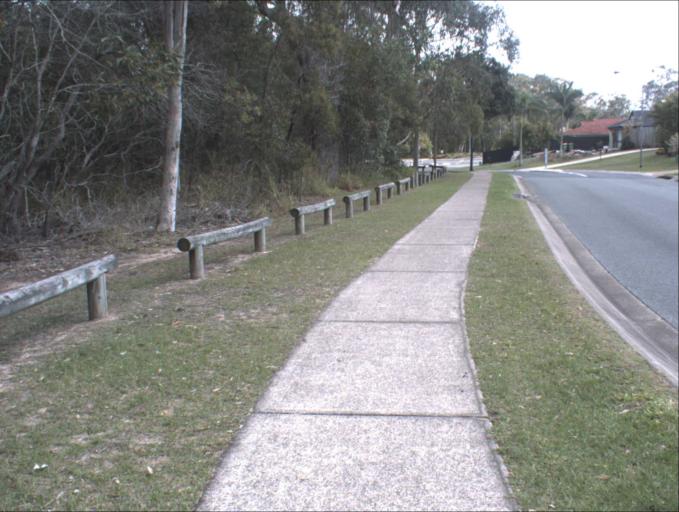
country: AU
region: Queensland
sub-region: Logan
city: Park Ridge South
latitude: -27.6823
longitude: 153.0400
